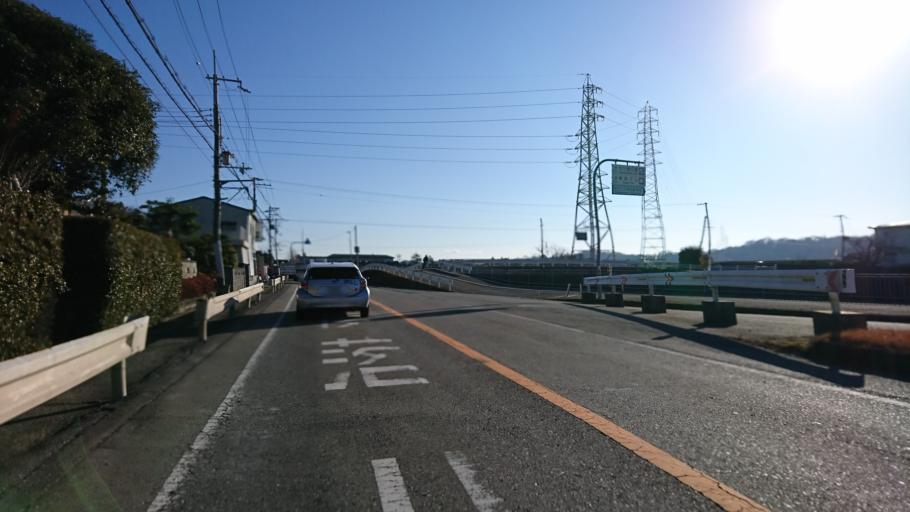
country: JP
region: Hyogo
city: Kakogawacho-honmachi
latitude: 34.7868
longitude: 134.8555
